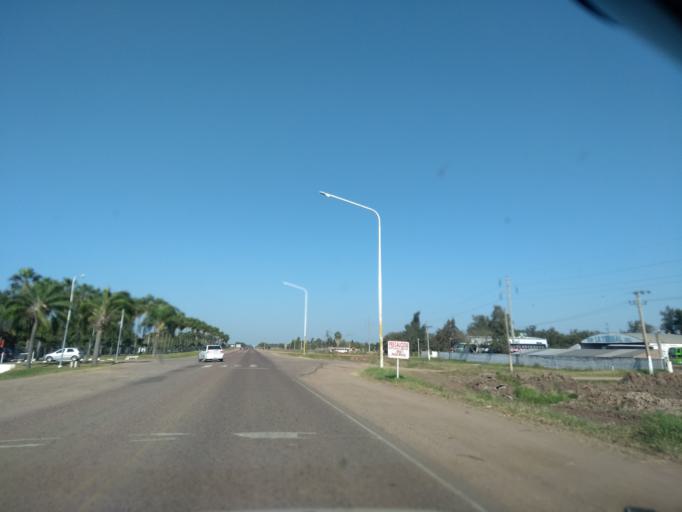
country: AR
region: Chaco
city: Presidencia Roque Saenz Pena
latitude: -26.8167
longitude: -60.4202
